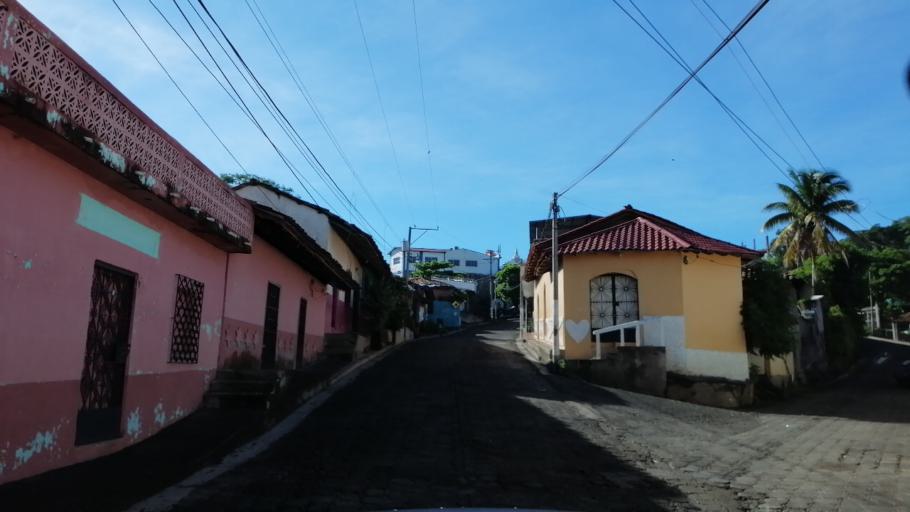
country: SV
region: Morazan
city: Cacaopera
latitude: 13.7744
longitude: -88.0805
